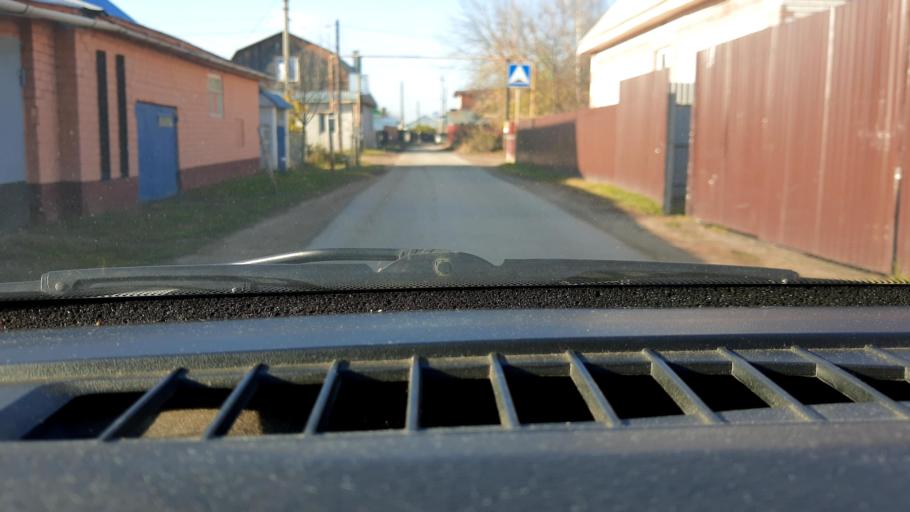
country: RU
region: Nizjnij Novgorod
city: Neklyudovo
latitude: 56.4133
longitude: 43.9786
